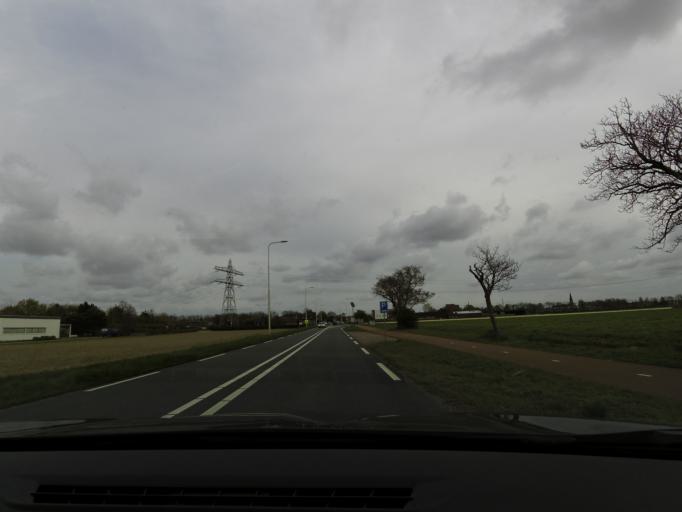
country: NL
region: South Holland
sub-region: Gemeente Teylingen
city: Sassenheim
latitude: 52.2351
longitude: 4.5156
